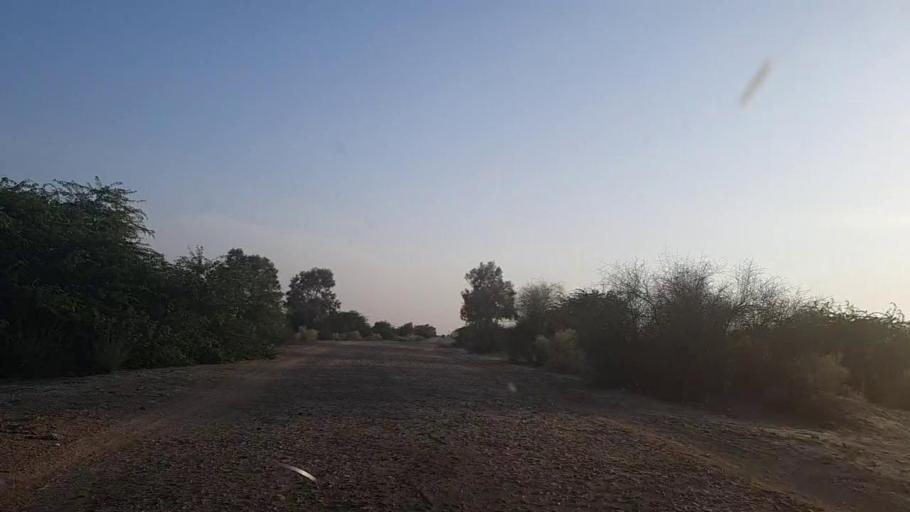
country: PK
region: Sindh
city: Khanpur
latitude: 27.6475
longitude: 69.4617
